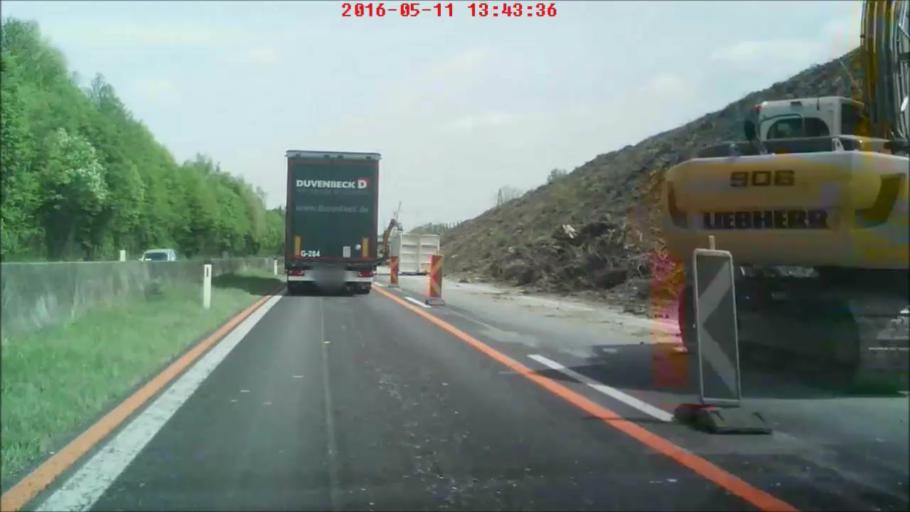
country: AT
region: Upper Austria
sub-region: Politischer Bezirk Ried im Innkreis
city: Ried im Innkreis
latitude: 48.2300
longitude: 13.5971
